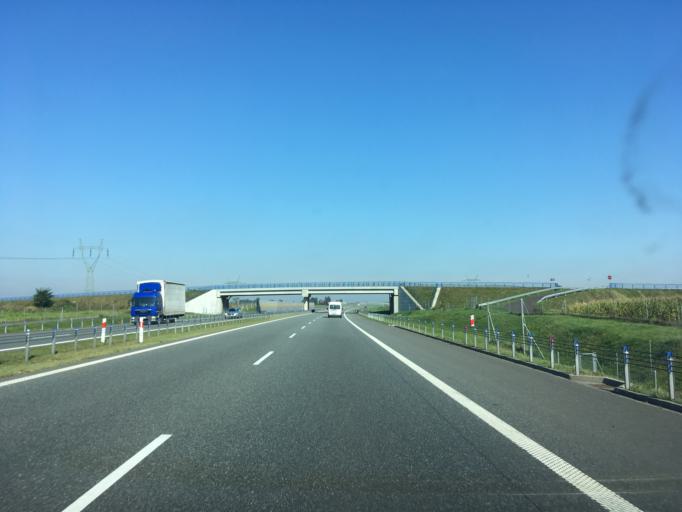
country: PL
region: Kujawsko-Pomorskie
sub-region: Powiat chelminski
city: Lisewo
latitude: 53.2285
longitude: 18.7281
